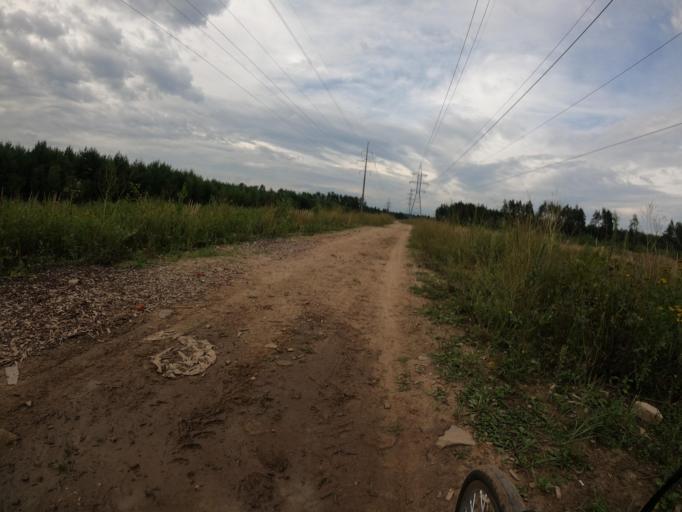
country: RU
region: Moskovskaya
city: Rodniki
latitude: 55.6768
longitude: 38.0856
